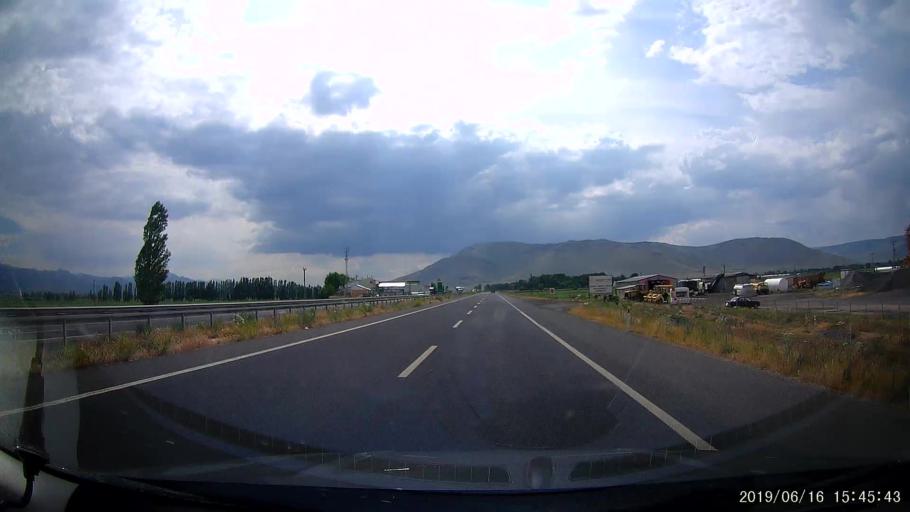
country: TR
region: Erzurum
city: Pasinler
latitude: 39.9891
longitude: 41.7599
